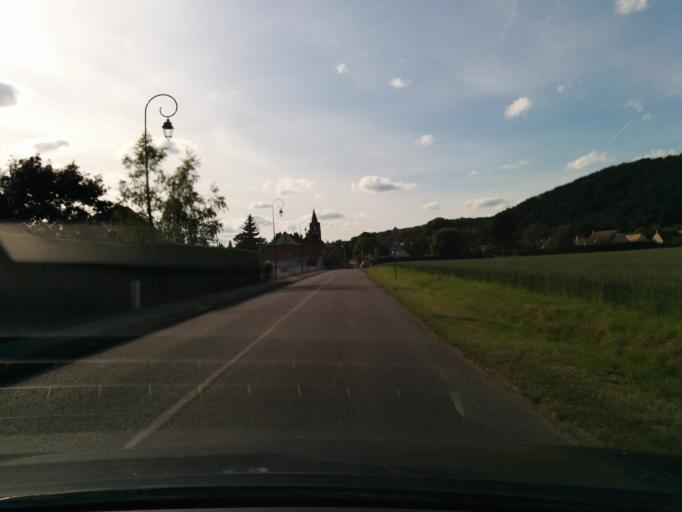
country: FR
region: Haute-Normandie
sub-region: Departement de l'Eure
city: Courcelles-sur-Seine
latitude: 49.1675
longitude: 1.4093
